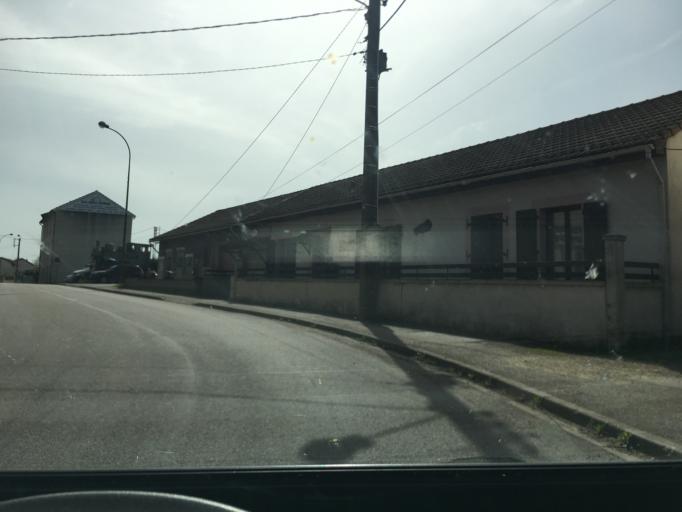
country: FR
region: Lorraine
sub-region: Departement de Meurthe-et-Moselle
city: Neuves-Maisons
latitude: 48.6154
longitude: 6.1112
